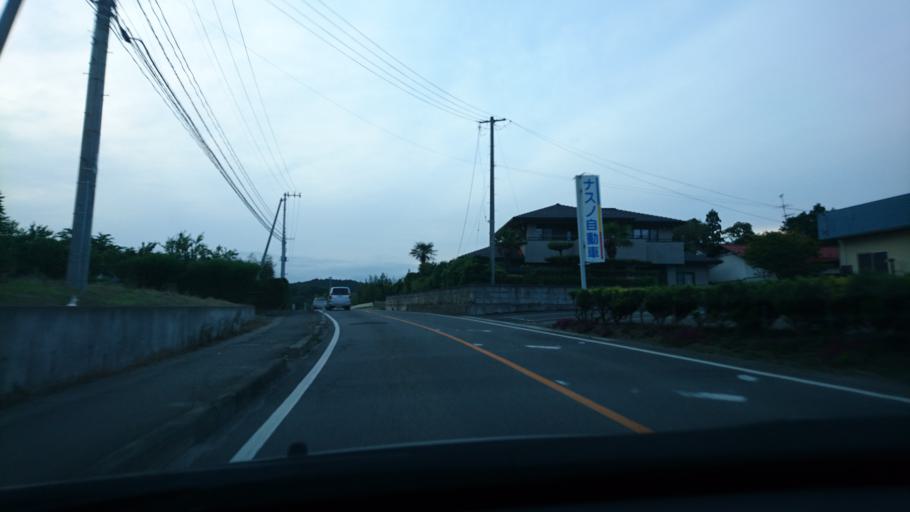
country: JP
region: Miyagi
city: Furukawa
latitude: 38.7555
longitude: 141.0068
